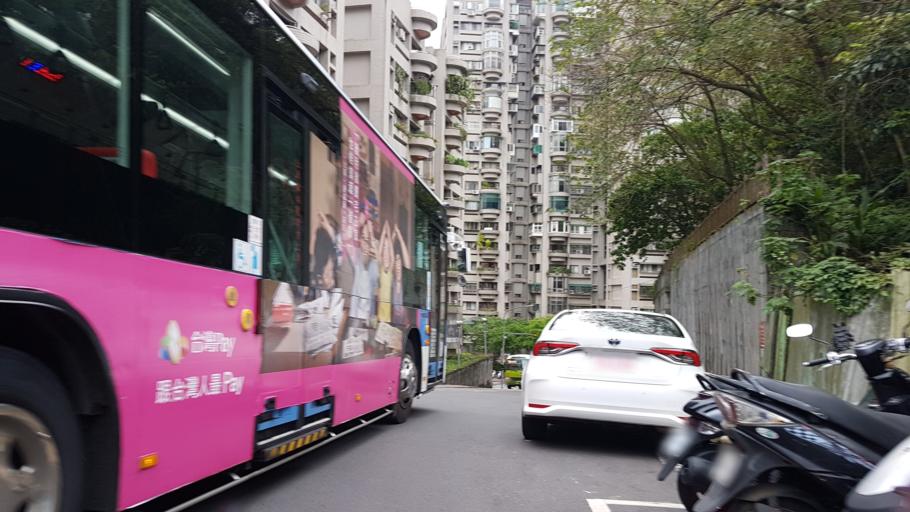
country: TW
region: Taipei
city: Taipei
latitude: 25.0380
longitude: 121.5915
